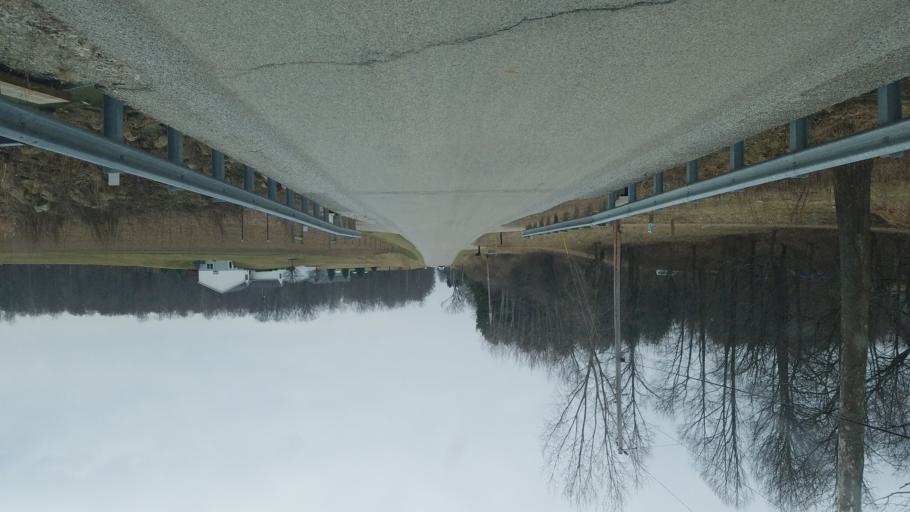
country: US
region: Ohio
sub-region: Morrow County
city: Mount Gilead
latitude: 40.6170
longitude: -82.8042
